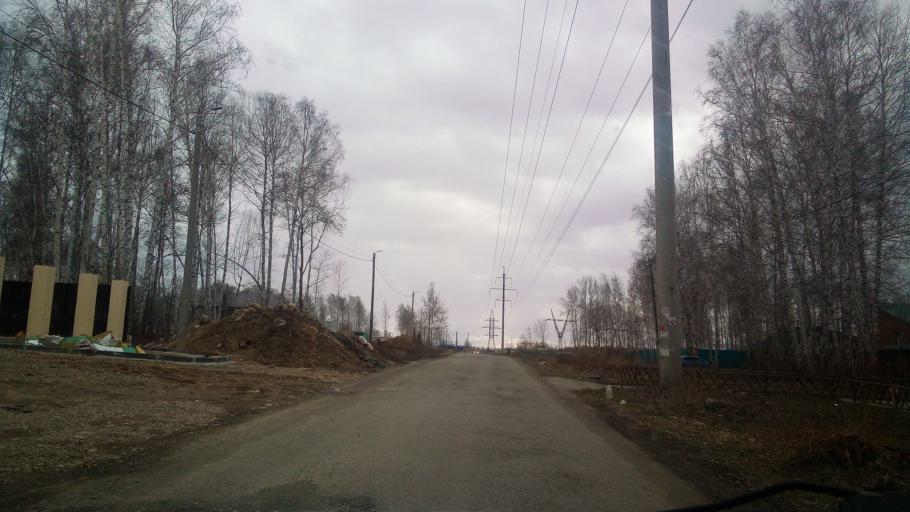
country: RU
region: Chelyabinsk
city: Sargazy
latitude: 55.1309
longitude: 61.2428
